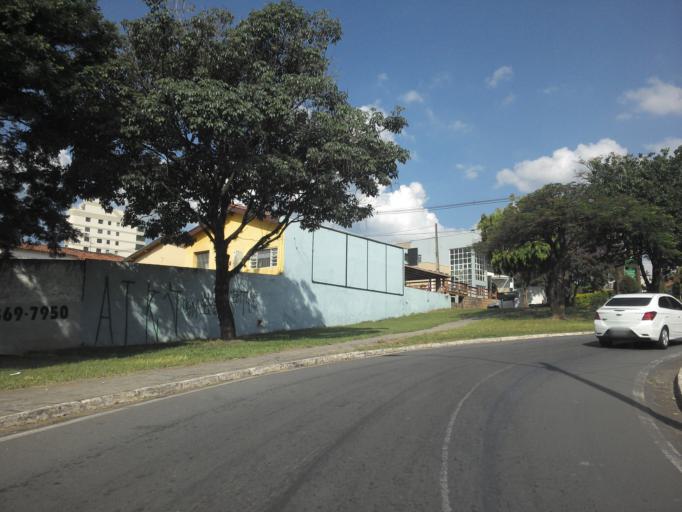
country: BR
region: Sao Paulo
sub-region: Valinhos
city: Valinhos
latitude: -22.9645
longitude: -47.0064
